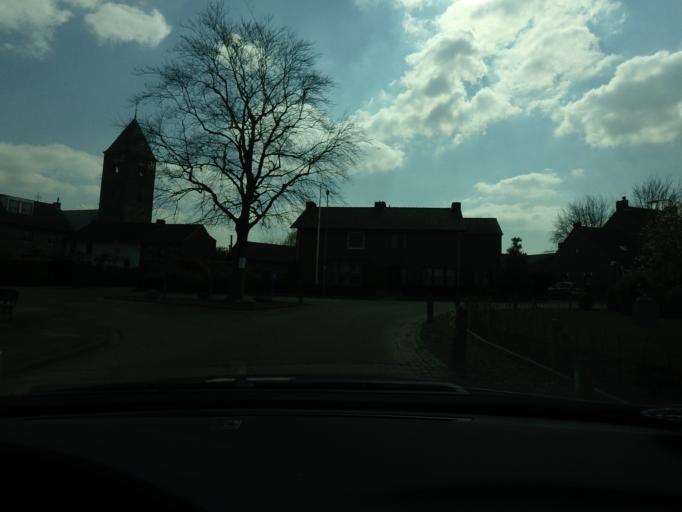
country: NL
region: Limburg
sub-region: Eijsden-Margraten
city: Eijsden
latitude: 50.7635
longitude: 5.7307
